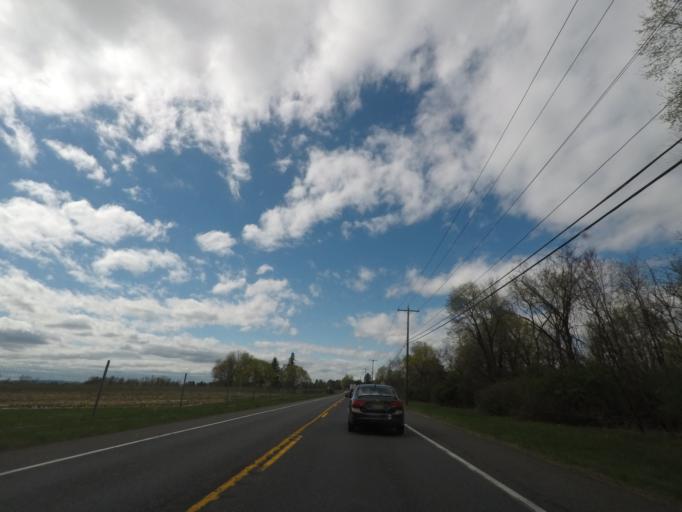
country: US
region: New York
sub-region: Columbia County
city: Niverville
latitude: 42.4473
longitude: -73.6885
